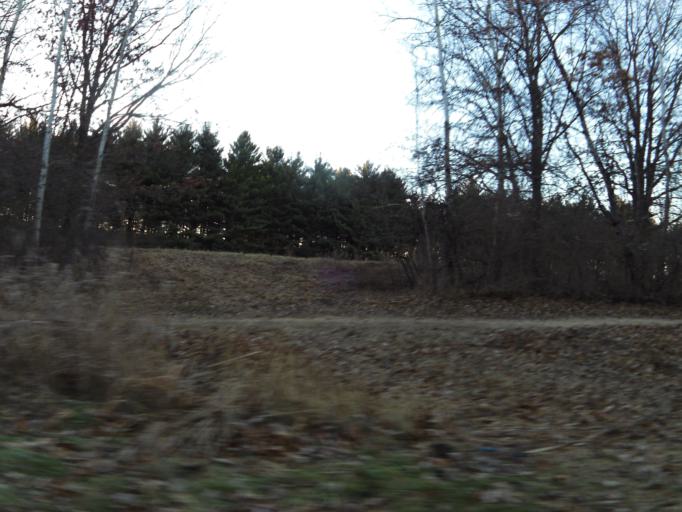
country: US
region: Minnesota
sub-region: Washington County
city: Grant
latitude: 45.0889
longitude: -92.8914
